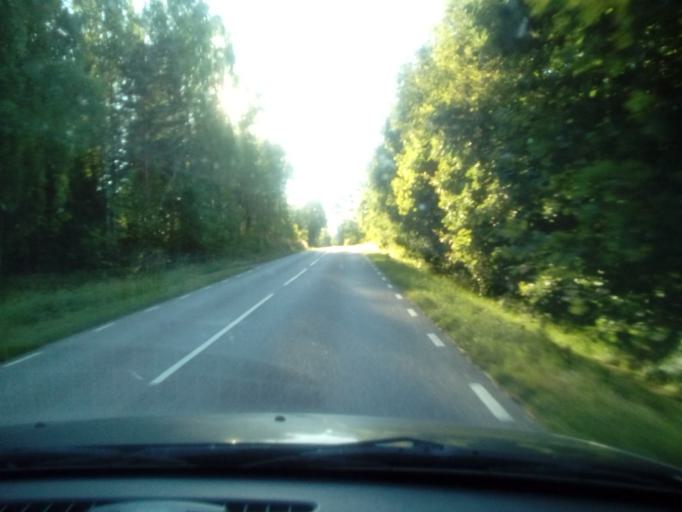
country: SE
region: Kalmar
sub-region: Vasterviks Kommun
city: Gamleby
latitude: 57.8184
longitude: 16.4707
